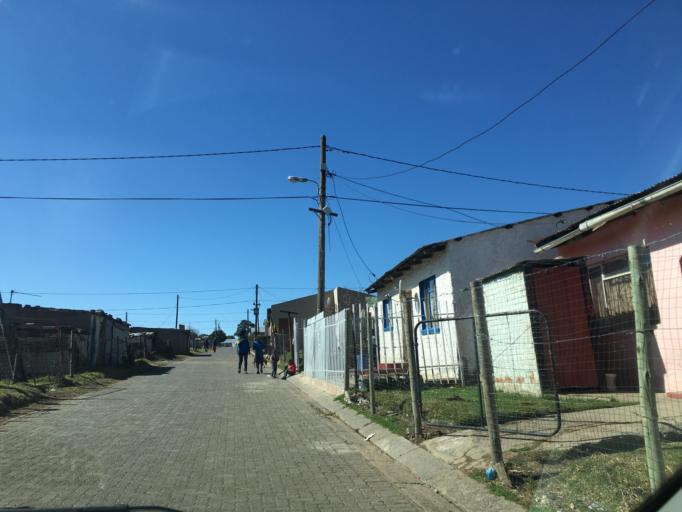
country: ZA
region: Eastern Cape
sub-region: Chris Hani District Municipality
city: Elliot
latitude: -31.3358
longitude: 27.8597
